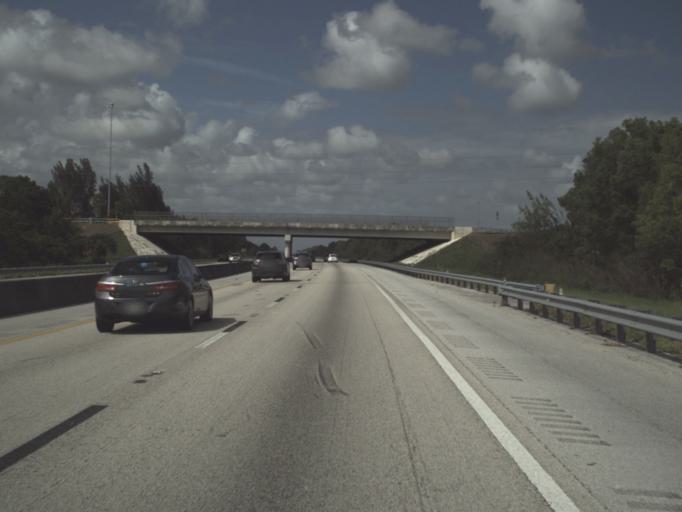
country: US
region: Florida
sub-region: Palm Beach County
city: Palm Beach Gardens
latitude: 26.8812
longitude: -80.1303
